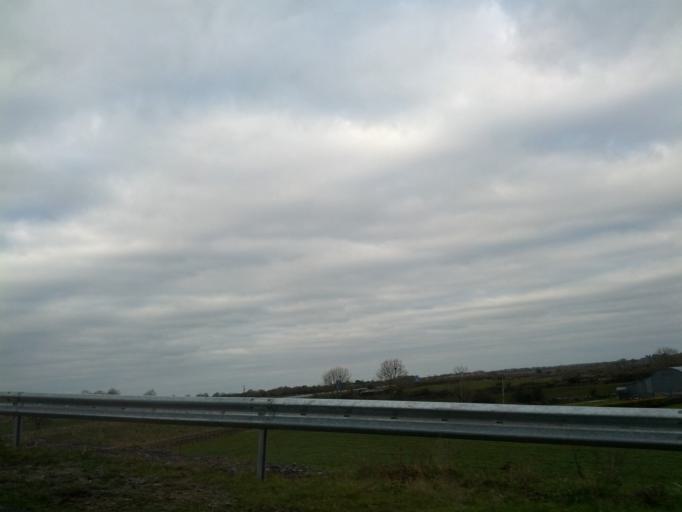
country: IE
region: Connaught
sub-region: County Galway
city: Gort
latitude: 53.1643
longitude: -8.8512
